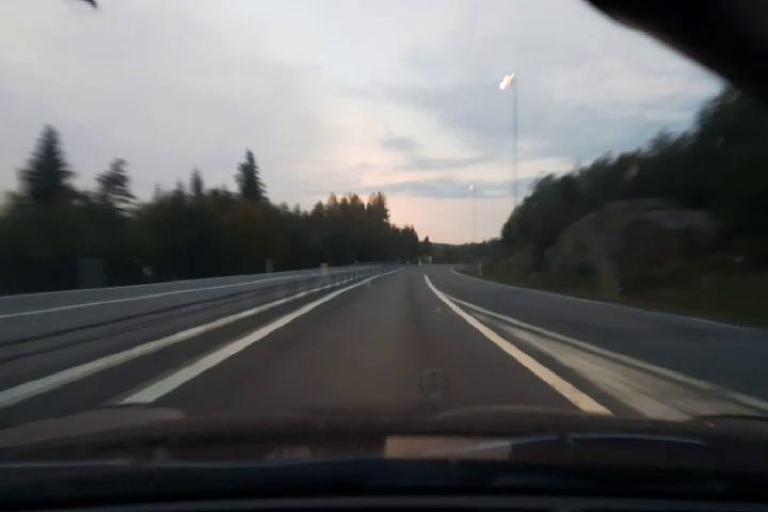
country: SE
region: Vaesternorrland
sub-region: Kramfors Kommun
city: Nordingra
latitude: 62.9411
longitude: 18.0943
